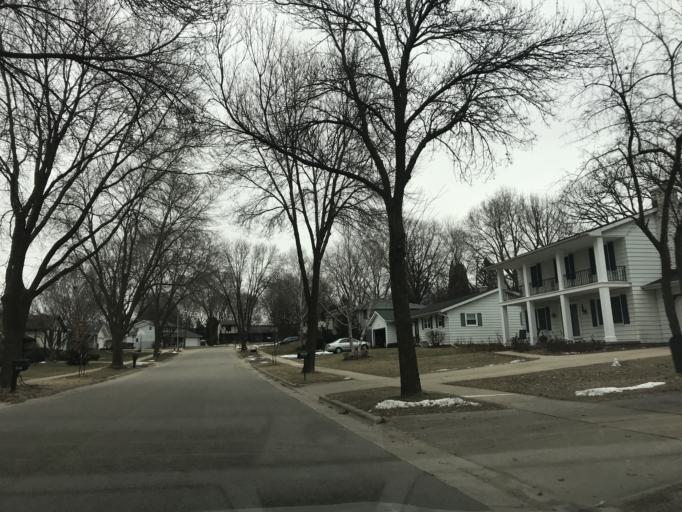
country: US
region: Wisconsin
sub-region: Dane County
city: Monona
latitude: 43.0922
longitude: -89.2893
